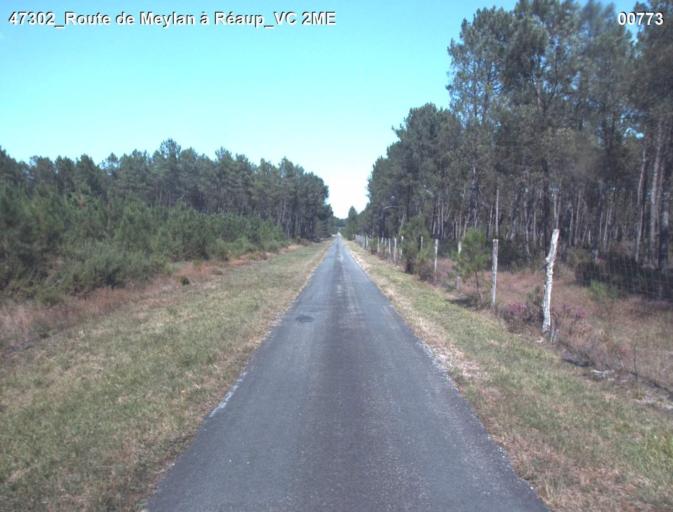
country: FR
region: Aquitaine
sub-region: Departement du Lot-et-Garonne
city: Mezin
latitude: 44.1016
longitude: 0.1364
